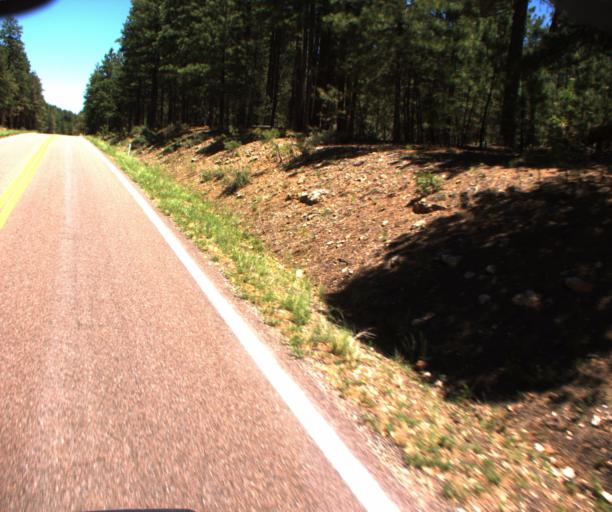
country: US
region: Arizona
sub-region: Gila County
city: Pine
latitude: 34.4462
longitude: -111.4502
